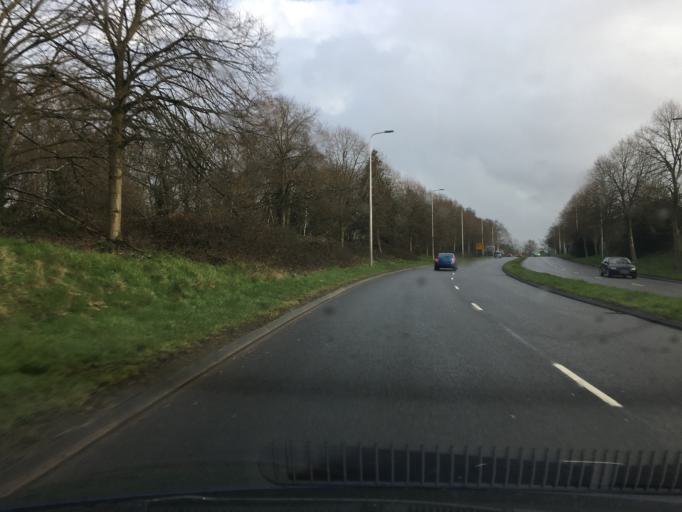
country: GB
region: England
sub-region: Bracknell Forest
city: Bracknell
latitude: 51.3999
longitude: -0.7618
